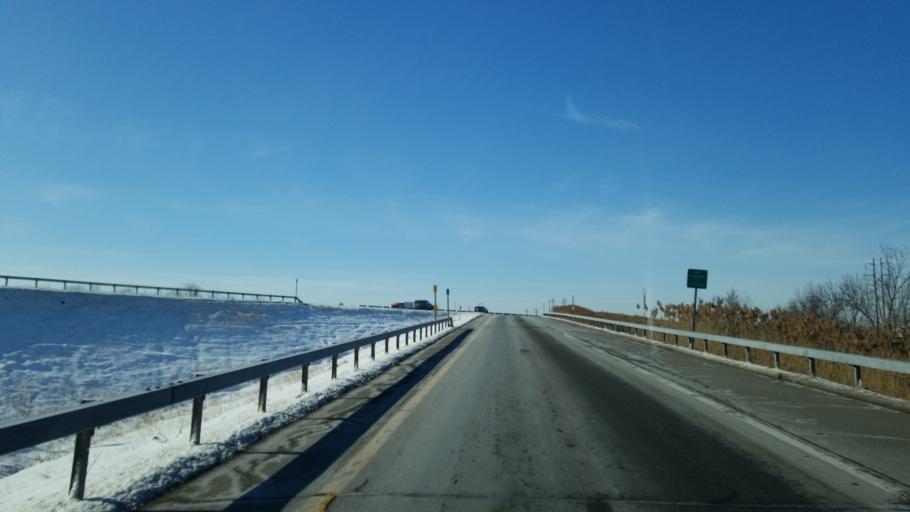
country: US
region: New York
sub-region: Erie County
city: Tonawanda
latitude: 42.9998
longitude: -78.8545
